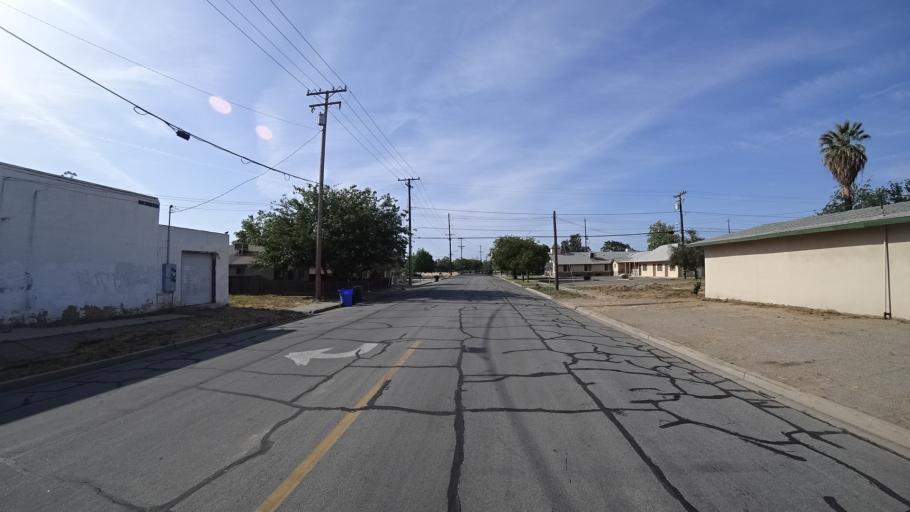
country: US
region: California
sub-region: Kings County
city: Hanford
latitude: 36.3221
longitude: -119.6464
